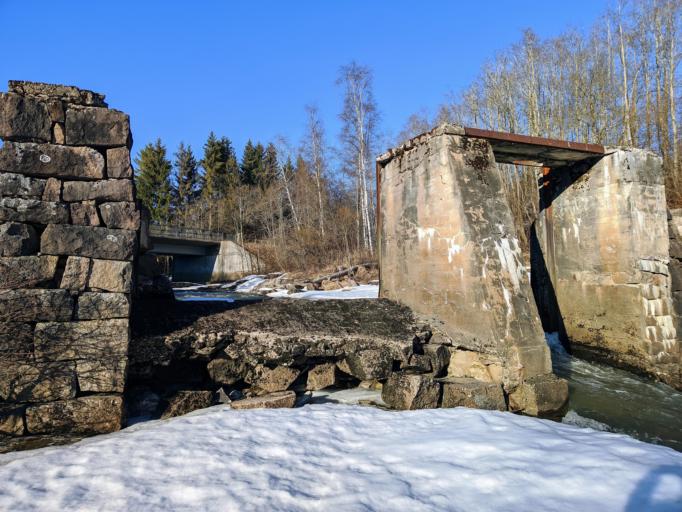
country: NO
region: Akershus
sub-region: Nannestad
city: Teigebyen
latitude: 60.2078
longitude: 10.9829
